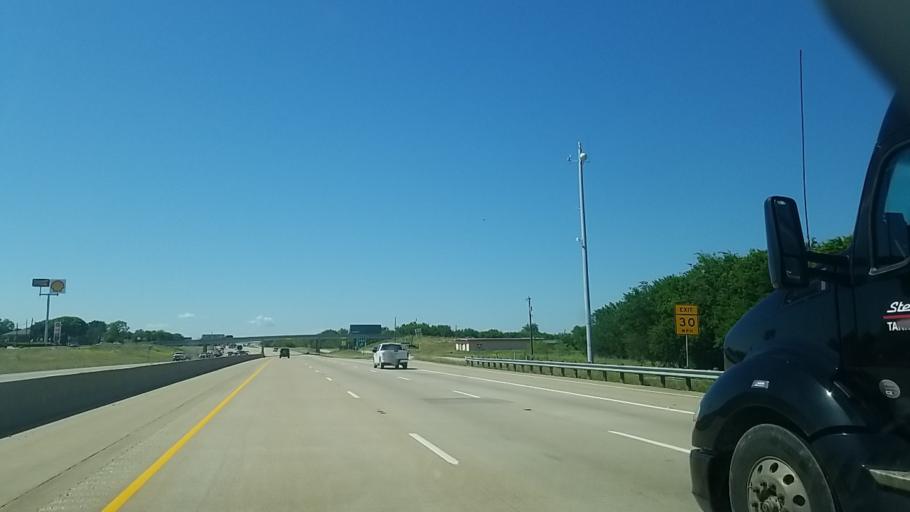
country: US
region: Texas
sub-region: Navarro County
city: Corsicana
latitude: 32.2421
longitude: -96.4951
